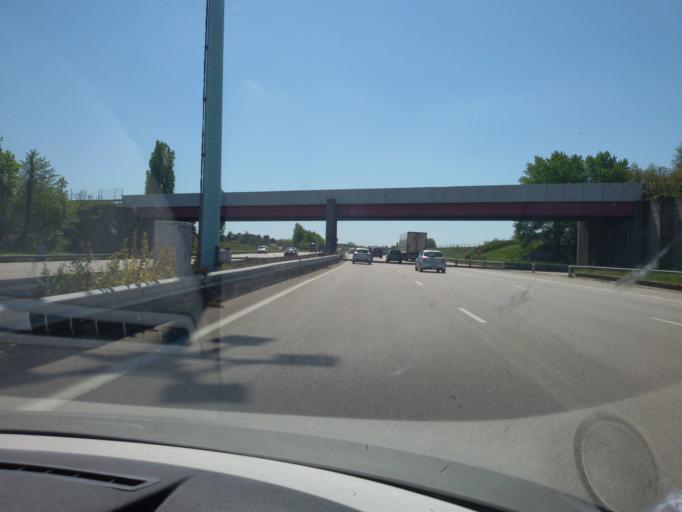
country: FR
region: Rhone-Alpes
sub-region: Departement de l'Isere
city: Reventin-Vaugris
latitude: 45.4733
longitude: 4.8329
